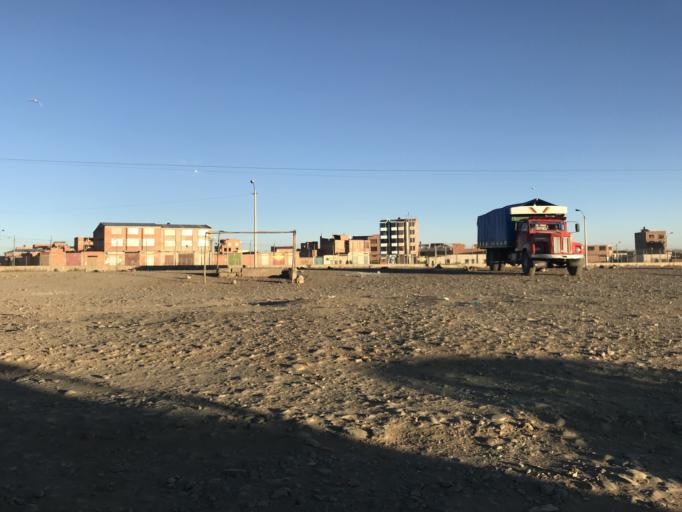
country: BO
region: La Paz
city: La Paz
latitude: -16.5003
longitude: -68.2363
